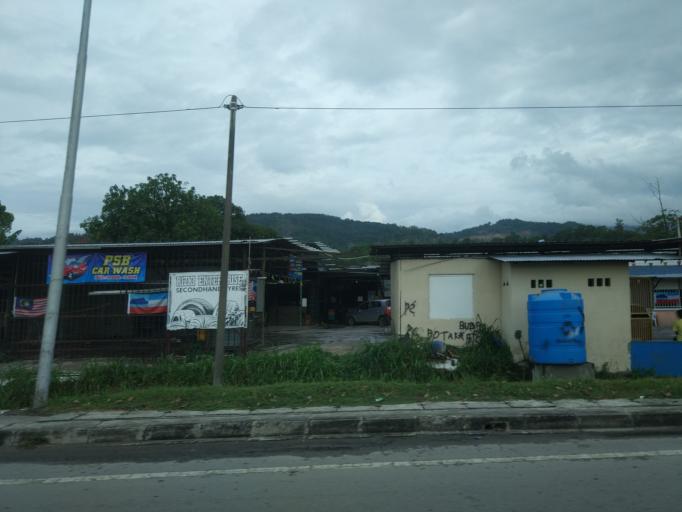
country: MY
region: Sabah
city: Kota Kinabalu
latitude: 6.1024
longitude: 116.2026
